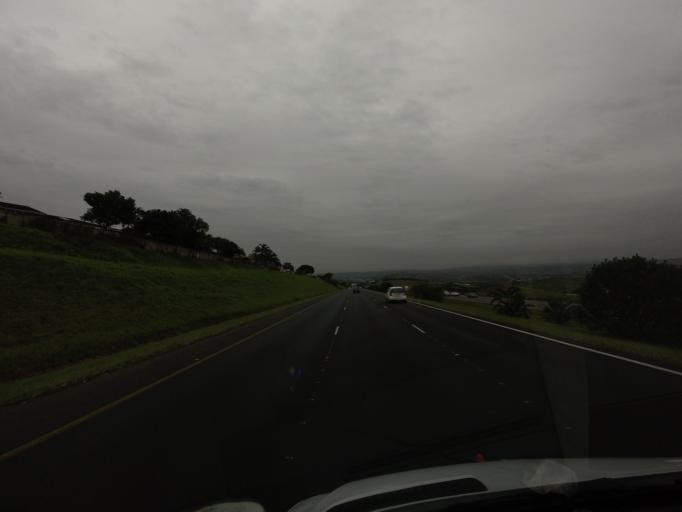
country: ZA
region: KwaZulu-Natal
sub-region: eThekwini Metropolitan Municipality
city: Durban
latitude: -29.7396
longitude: 31.0471
